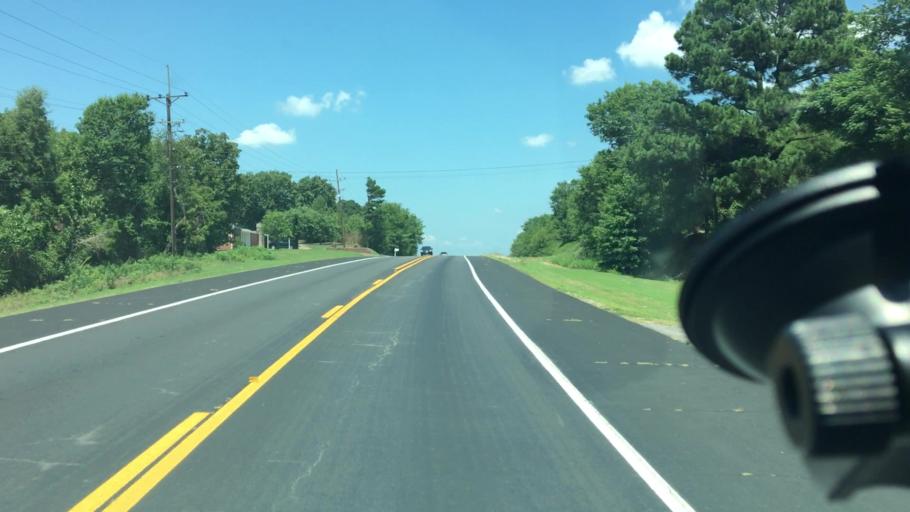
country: US
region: Arkansas
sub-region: Sebastian County
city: Lavaca
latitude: 35.2995
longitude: -94.1575
